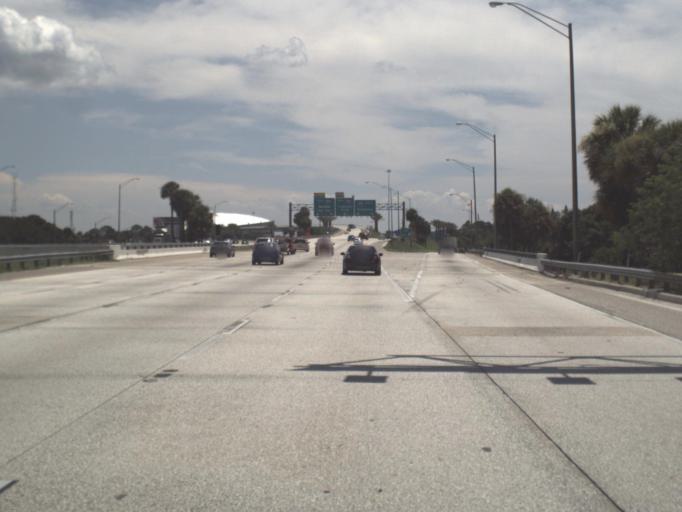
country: US
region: Florida
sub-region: Pinellas County
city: Saint Petersburg
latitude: 27.7818
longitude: -82.6613
